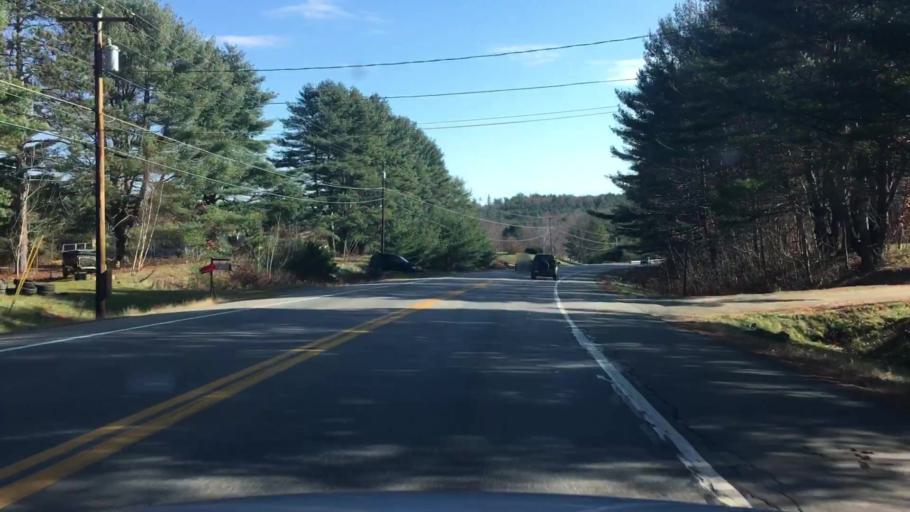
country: US
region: Maine
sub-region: Kennebec County
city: Windsor
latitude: 44.2683
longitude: -69.5674
